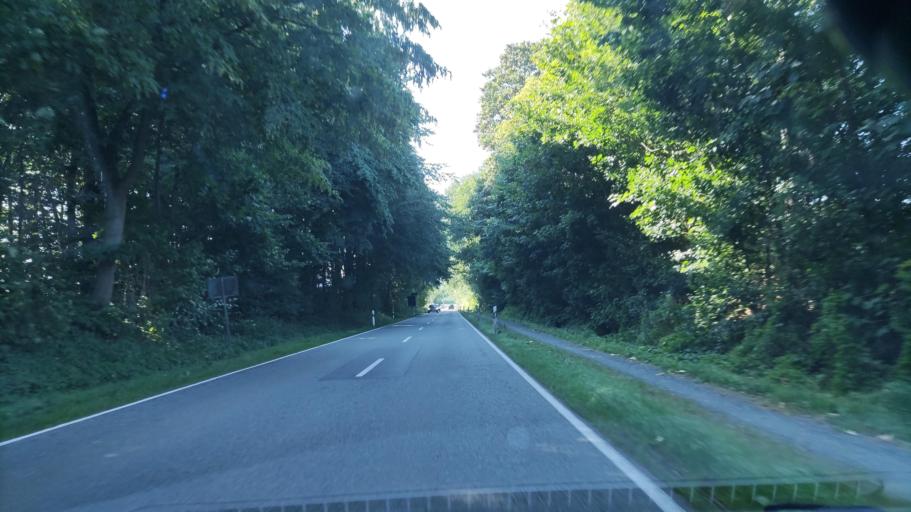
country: DE
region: Schleswig-Holstein
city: Hutten
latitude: 54.4310
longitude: 9.7274
